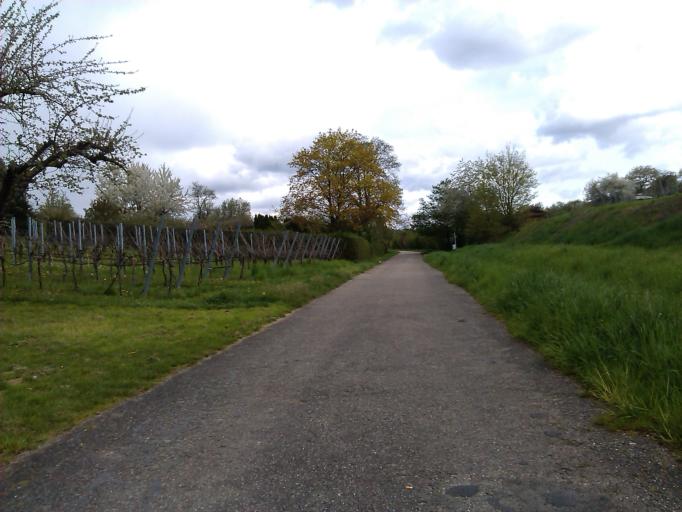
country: DE
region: Baden-Wuerttemberg
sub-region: Regierungsbezirk Stuttgart
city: Nordheim
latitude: 49.1029
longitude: 9.1389
